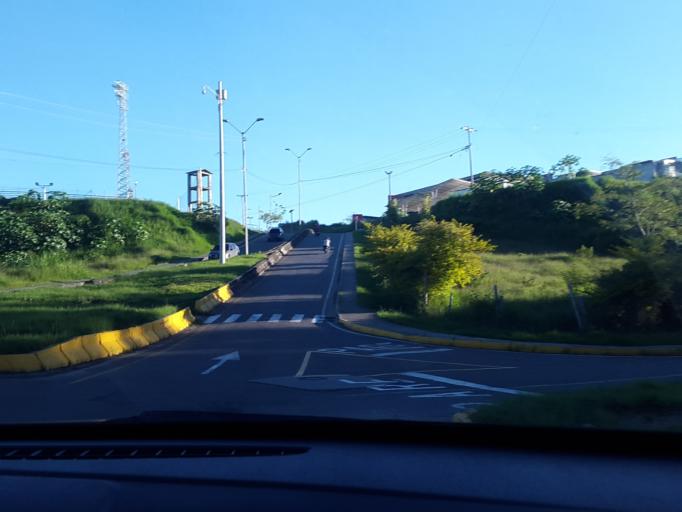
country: CO
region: Quindio
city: Armenia
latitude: 4.5383
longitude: -75.6850
